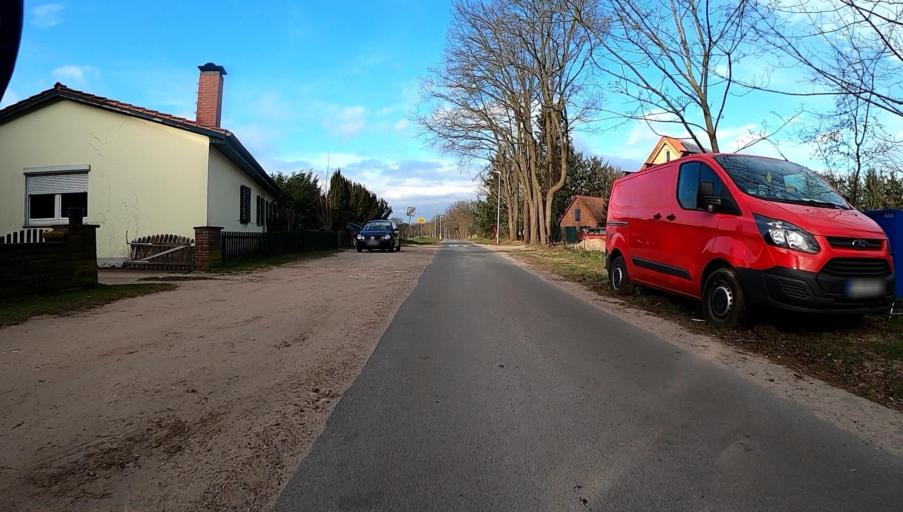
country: DE
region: Lower Saxony
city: Lindwedel
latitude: 52.5433
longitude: 9.6309
